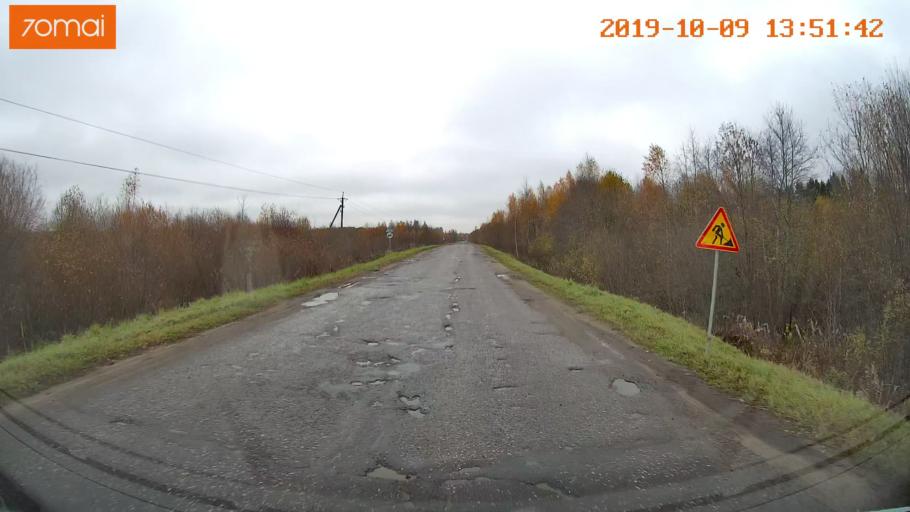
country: RU
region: Kostroma
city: Buy
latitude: 58.4089
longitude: 41.2413
